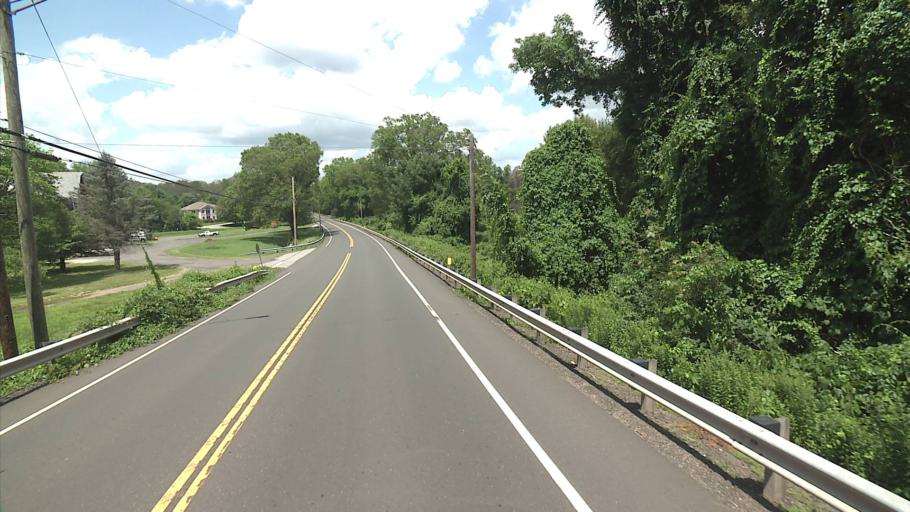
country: US
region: Connecticut
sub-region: Middlesex County
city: Higganum
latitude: 41.4834
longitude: -72.5173
